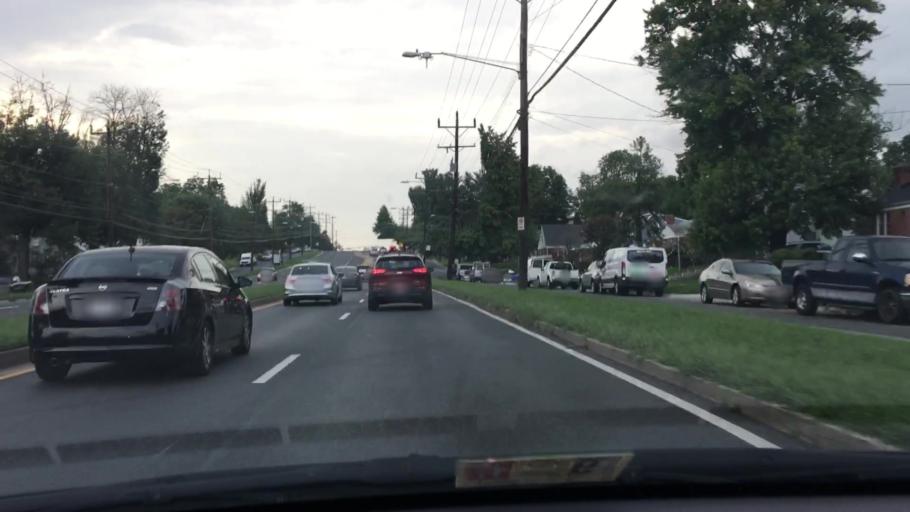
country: US
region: Maryland
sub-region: Montgomery County
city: North Kensington
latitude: 39.0538
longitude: -77.0780
